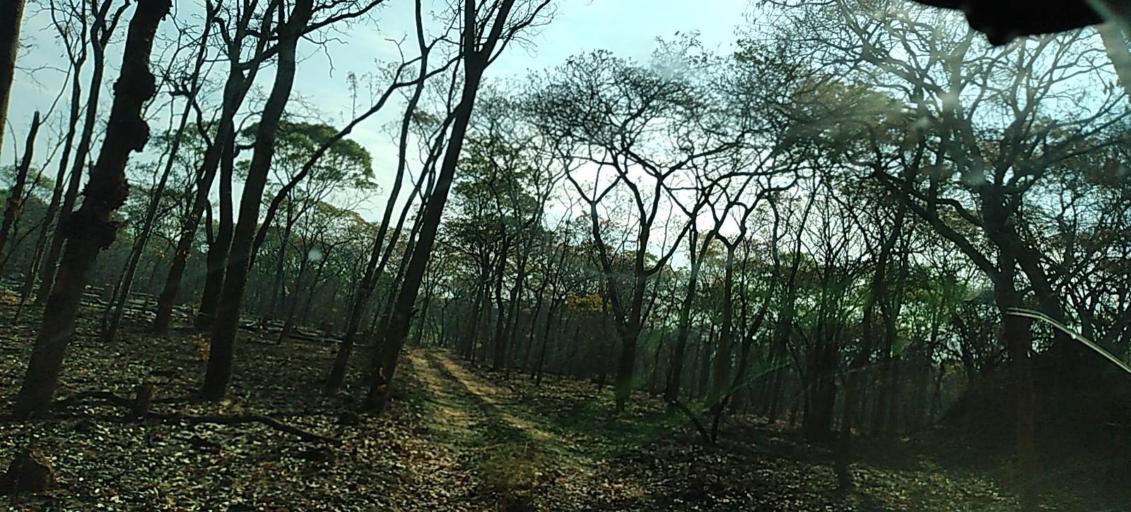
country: ZM
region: North-Western
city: Kalengwa
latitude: -13.2311
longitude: 25.0745
